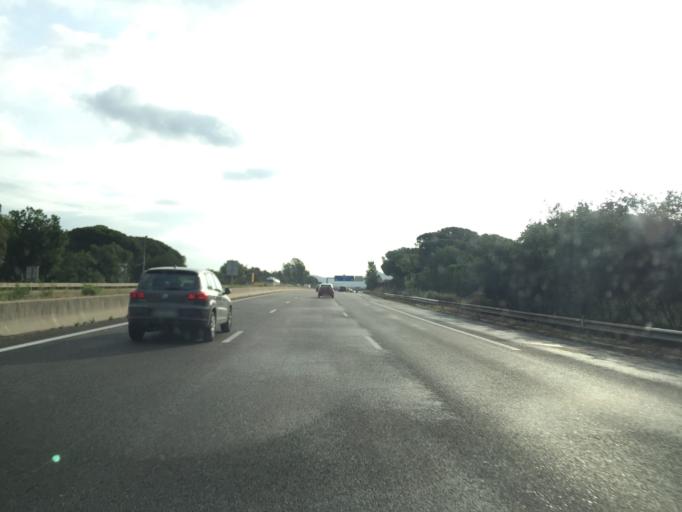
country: FR
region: Provence-Alpes-Cote d'Azur
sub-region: Departement du Var
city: Frejus
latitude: 43.4650
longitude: 6.7189
